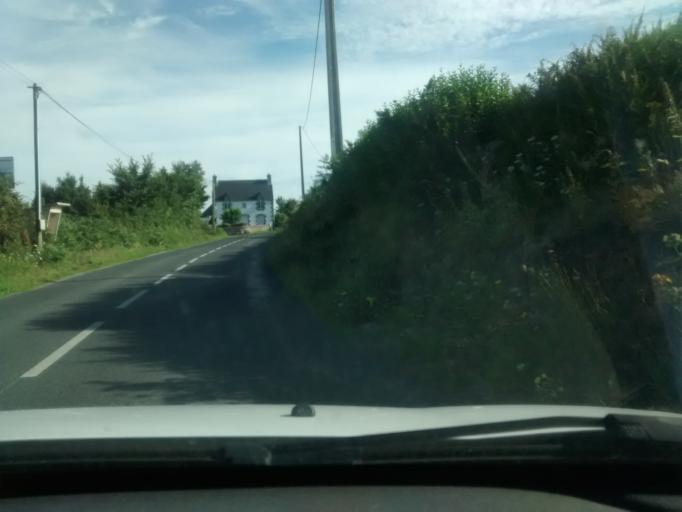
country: FR
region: Brittany
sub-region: Departement des Cotes-d'Armor
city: Plougrescant
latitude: 48.8326
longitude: -3.2353
